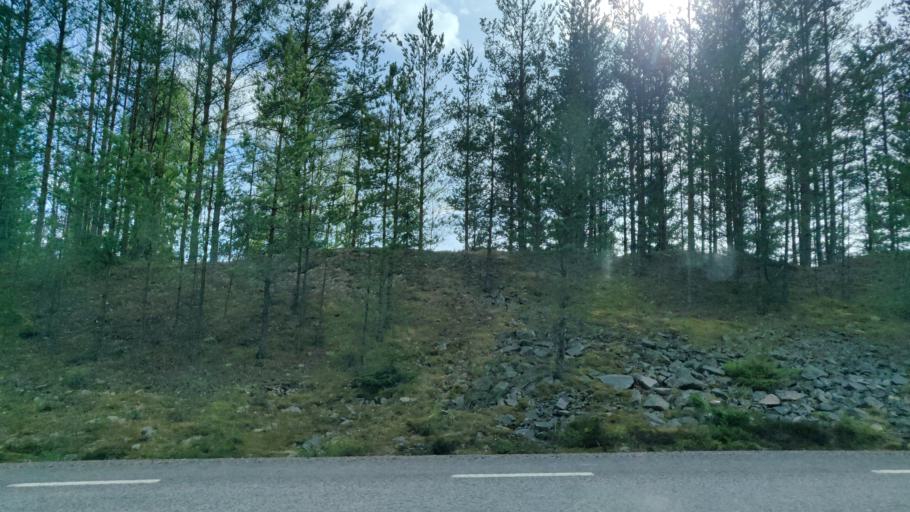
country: SE
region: Vaermland
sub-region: Forshaga Kommun
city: Deje
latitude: 59.5816
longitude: 13.4640
